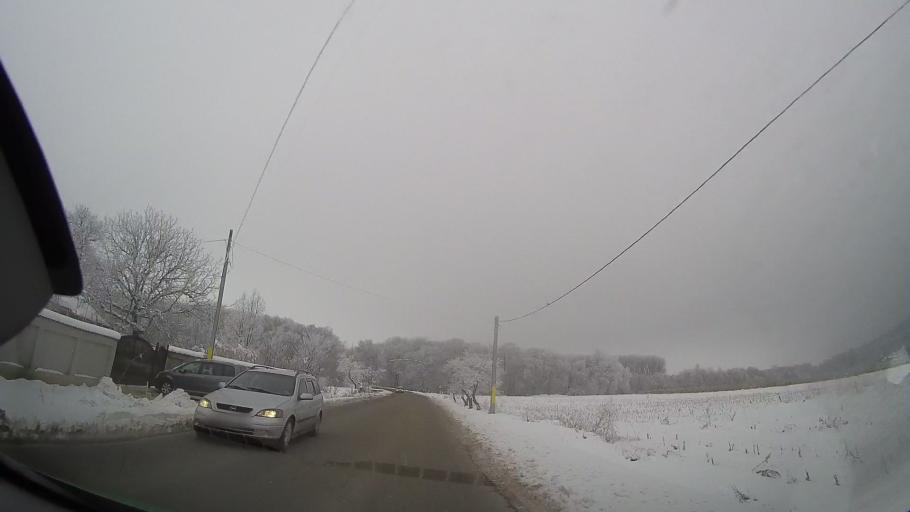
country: RO
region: Neamt
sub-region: Comuna Horia
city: Cotu Vames
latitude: 46.8796
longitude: 26.9740
